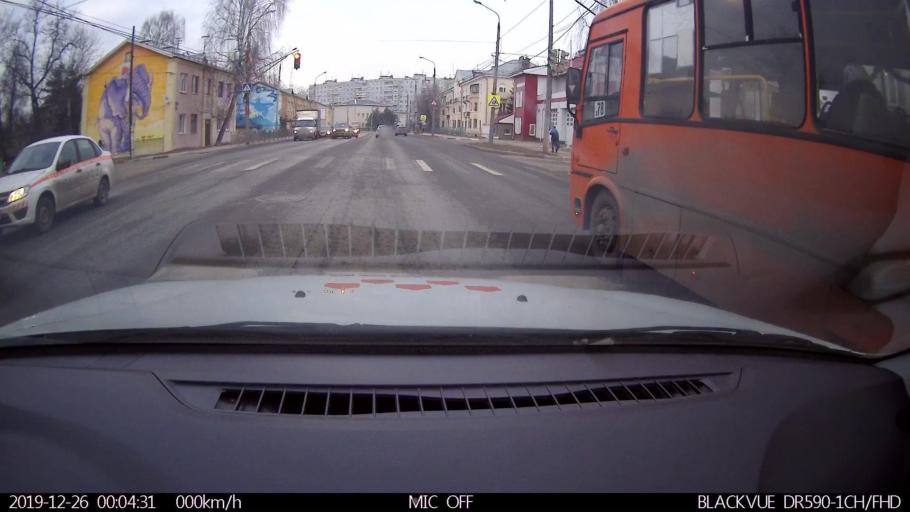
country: RU
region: Nizjnij Novgorod
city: Gorbatovka
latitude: 56.3473
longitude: 43.8459
